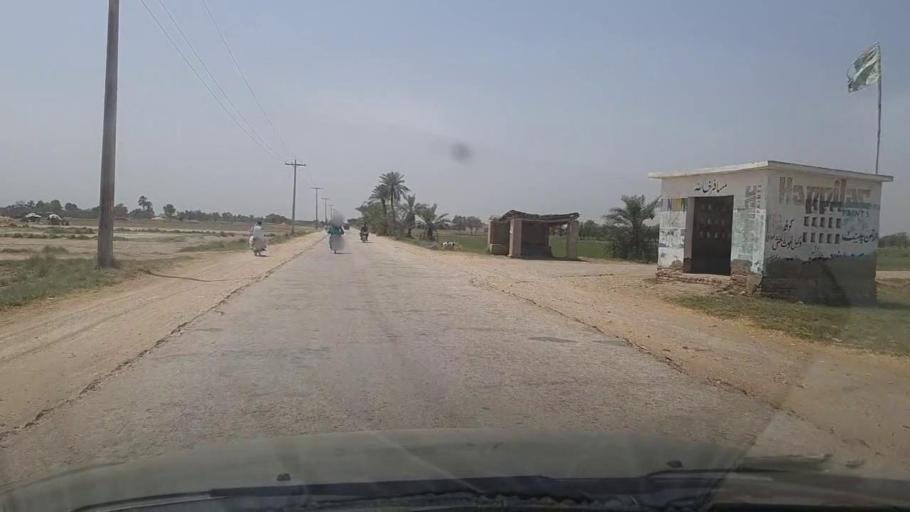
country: PK
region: Sindh
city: Bhiria
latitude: 26.8920
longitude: 68.2531
